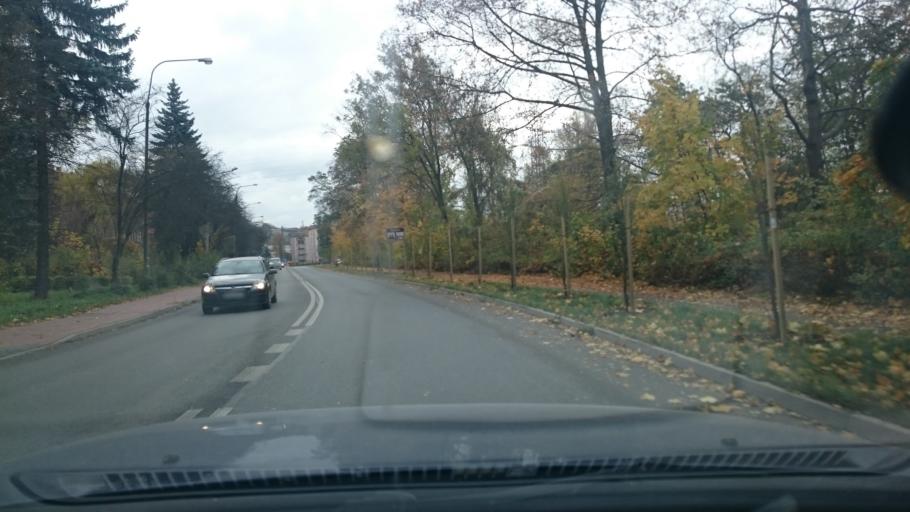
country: PL
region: Silesian Voivodeship
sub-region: Powiat bedzinski
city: Strzyzowice
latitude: 50.3523
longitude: 19.0787
